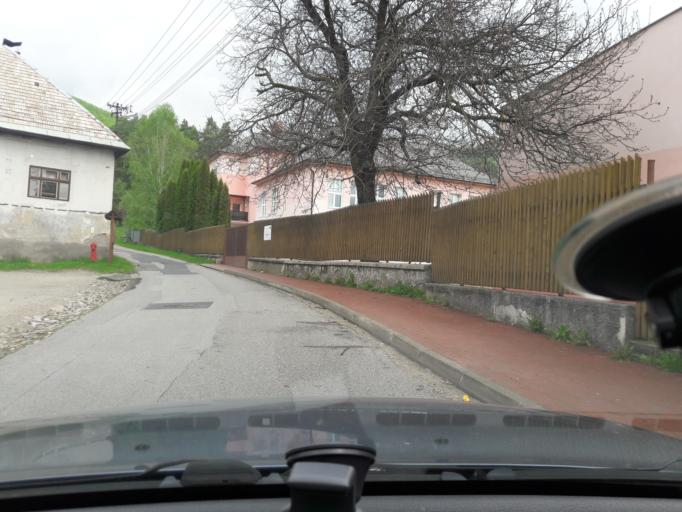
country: SK
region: Banskobystricky
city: Revuca
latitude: 48.7411
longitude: 20.0469
